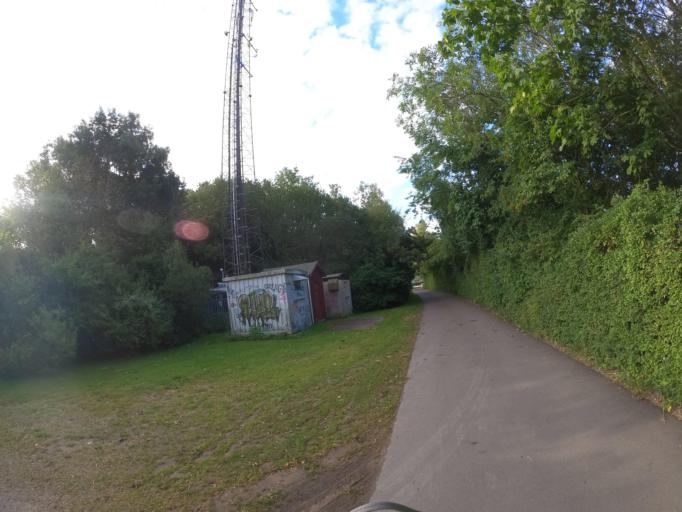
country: SE
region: Skane
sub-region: Staffanstorps Kommun
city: Staffanstorp
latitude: 55.6556
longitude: 13.2136
